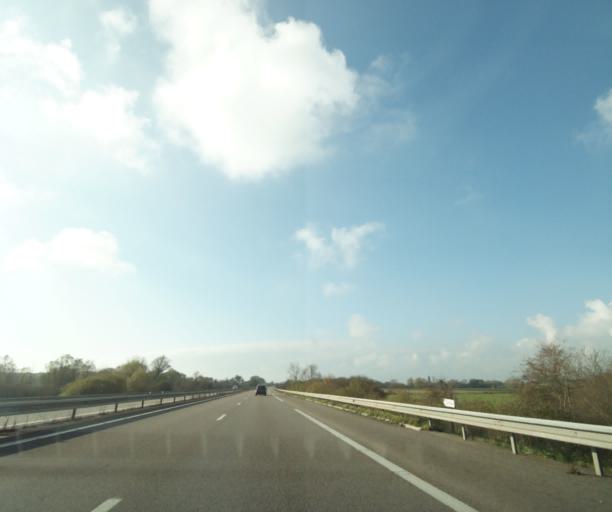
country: FR
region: Lorraine
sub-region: Departement de Meurthe-et-Moselle
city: Conflans-en-Jarnisy
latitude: 49.1597
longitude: 5.7408
